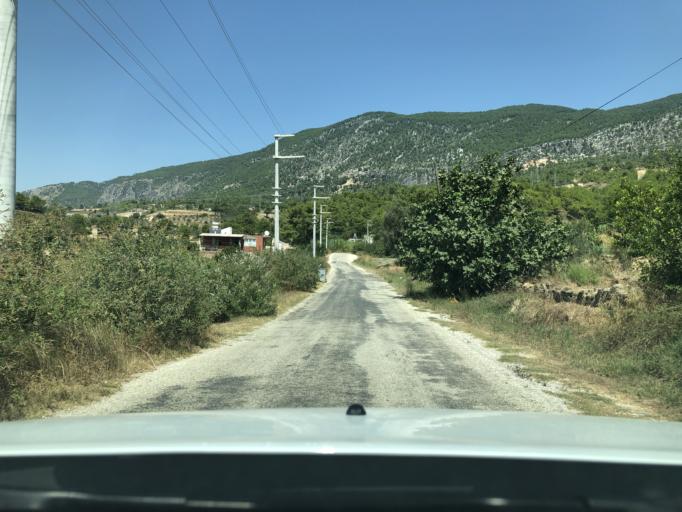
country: TR
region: Antalya
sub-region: Manavgat
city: Kizilagac
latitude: 36.8586
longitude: 31.5633
